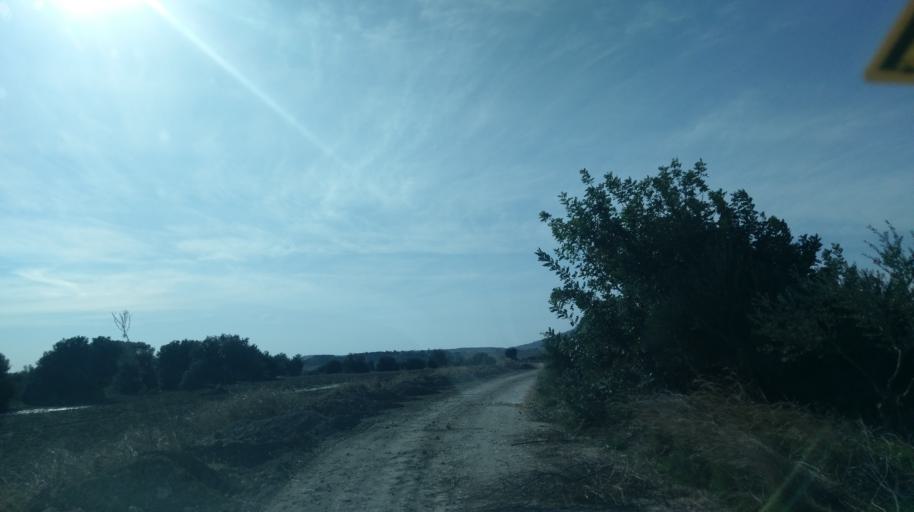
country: CY
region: Ammochostos
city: Trikomo
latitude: 35.3355
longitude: 33.8420
